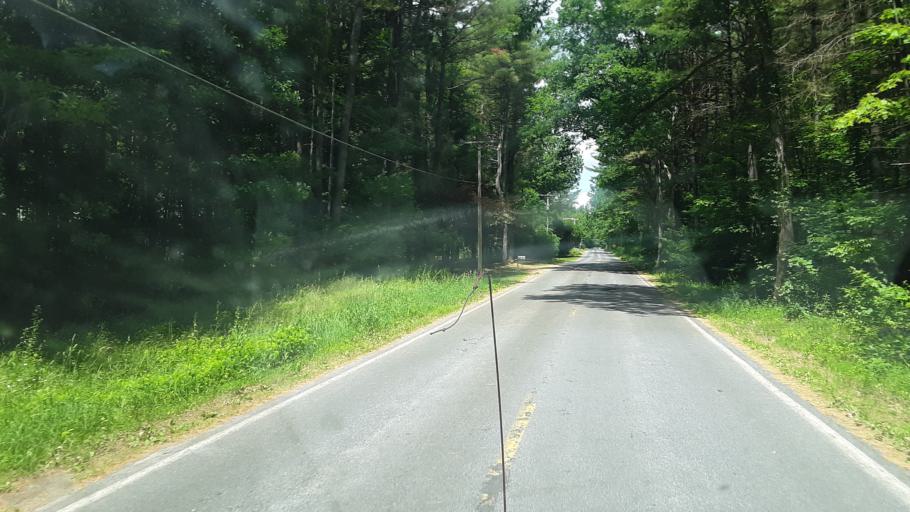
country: US
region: New York
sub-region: Oneida County
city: Rome
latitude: 43.2484
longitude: -75.5969
